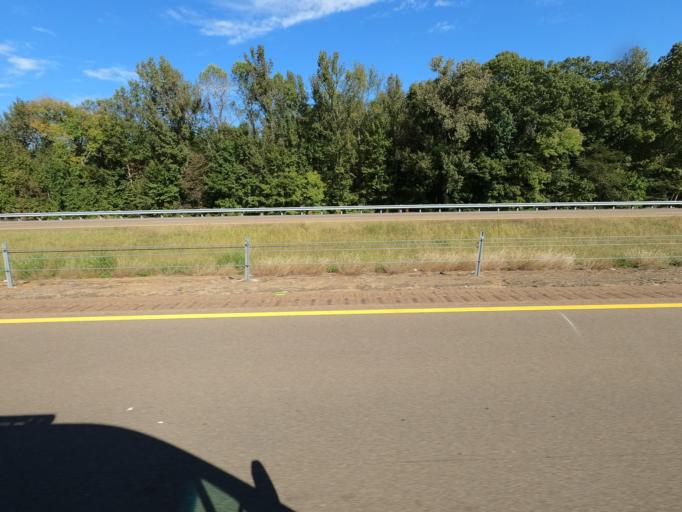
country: US
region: Tennessee
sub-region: Shelby County
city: Arlington
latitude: 35.3116
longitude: -89.7179
